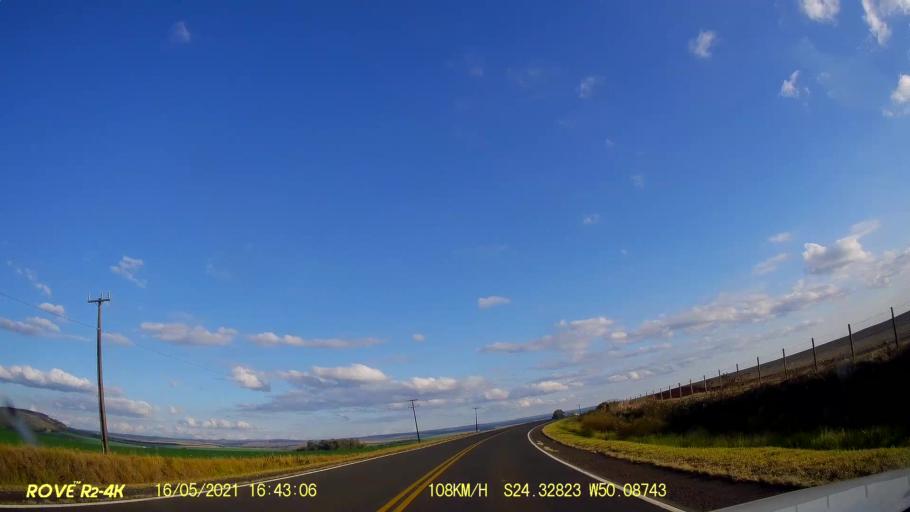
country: BR
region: Parana
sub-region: Pirai Do Sul
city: Pirai do Sul
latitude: -24.3286
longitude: -50.0875
